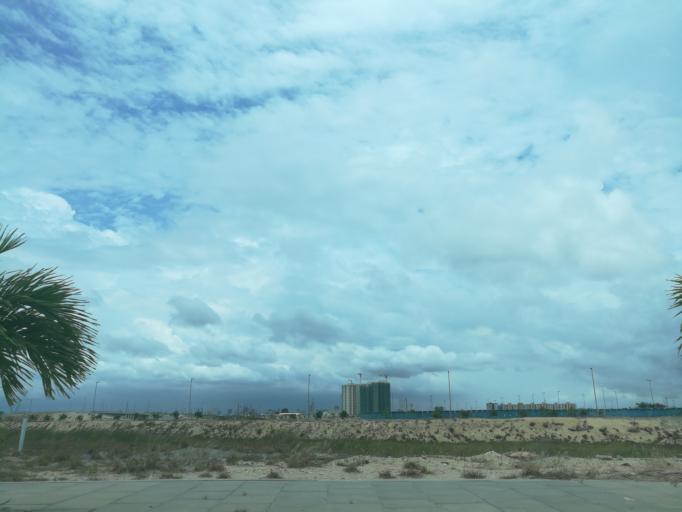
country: NG
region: Lagos
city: Ikoyi
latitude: 6.4097
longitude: 3.4143
